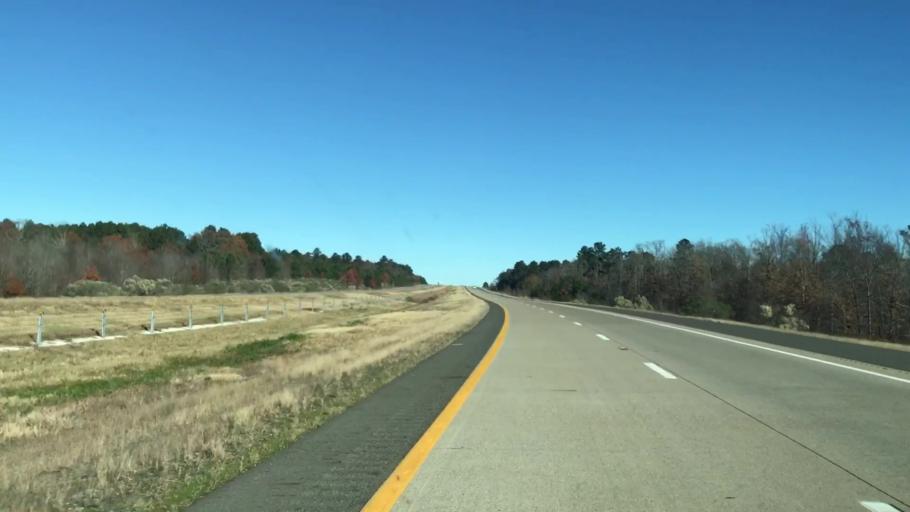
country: US
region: Texas
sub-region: Cass County
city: Queen City
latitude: 33.1714
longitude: -93.8779
